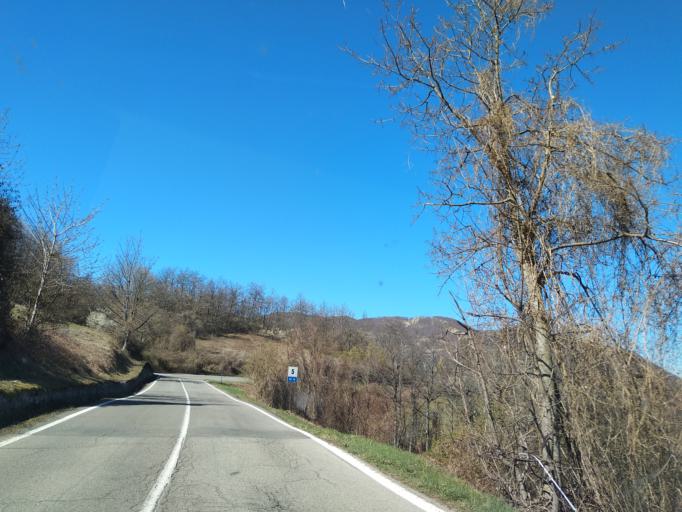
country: IT
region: Emilia-Romagna
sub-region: Provincia di Reggio Emilia
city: Ramiseto
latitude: 44.4144
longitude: 10.2913
